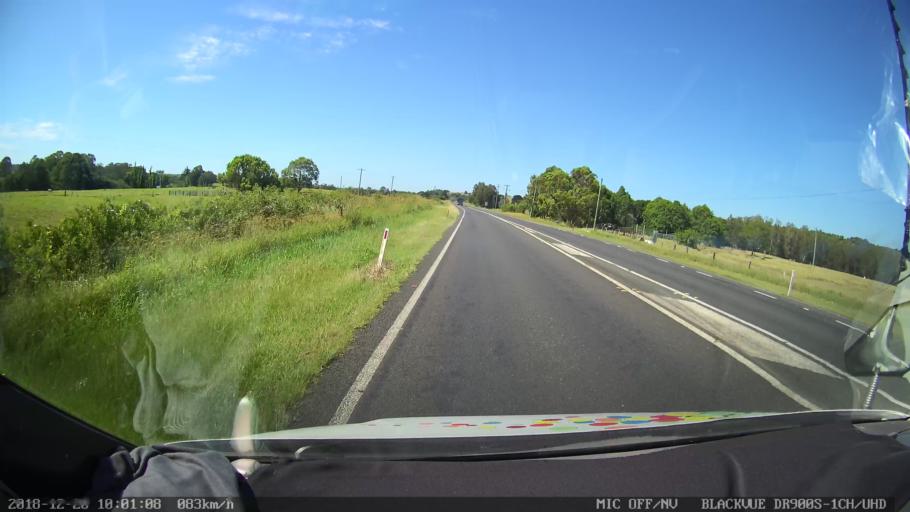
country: AU
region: New South Wales
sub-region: Lismore Municipality
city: Lismore
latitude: -28.8406
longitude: 153.2633
